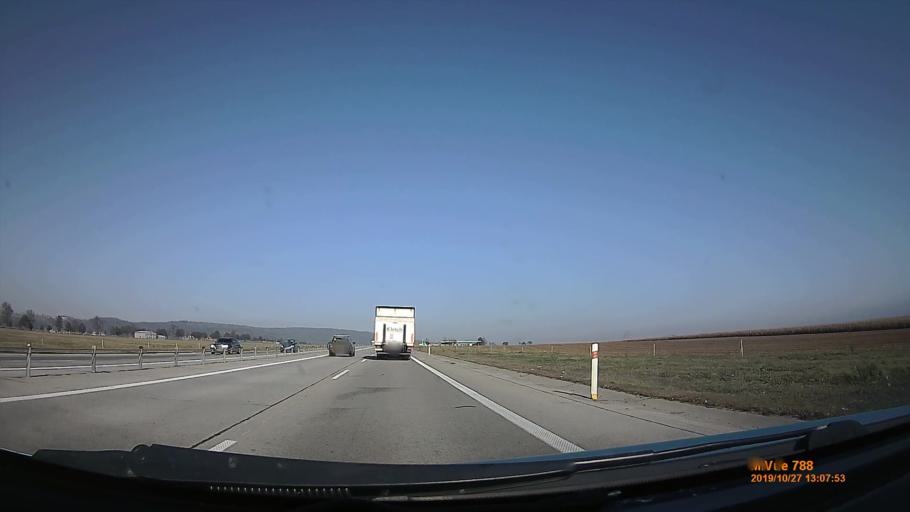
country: CZ
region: South Moravian
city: Pustimer
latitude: 49.3010
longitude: 17.0270
